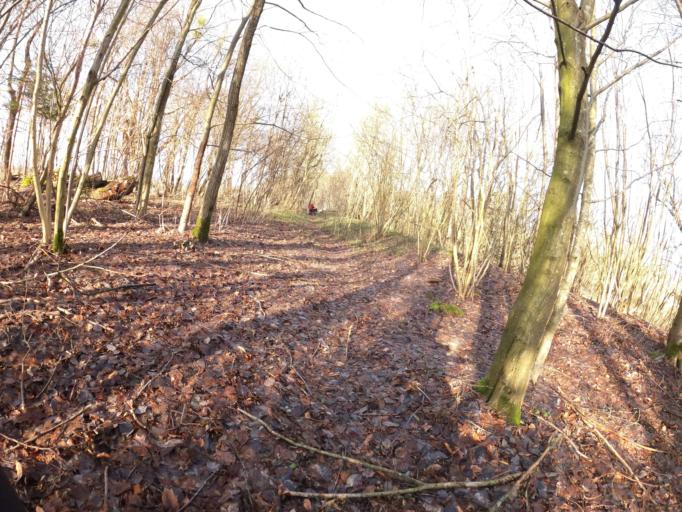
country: PL
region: West Pomeranian Voivodeship
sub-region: Powiat koszalinski
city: Polanow
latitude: 54.1454
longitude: 16.7673
